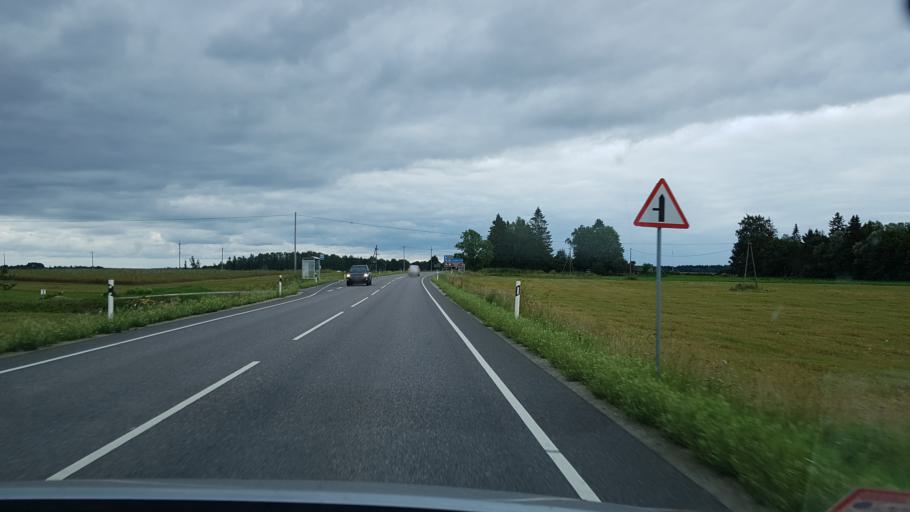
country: EE
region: Tartu
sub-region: Tartu linn
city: Tartu
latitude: 58.4196
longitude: 26.8709
